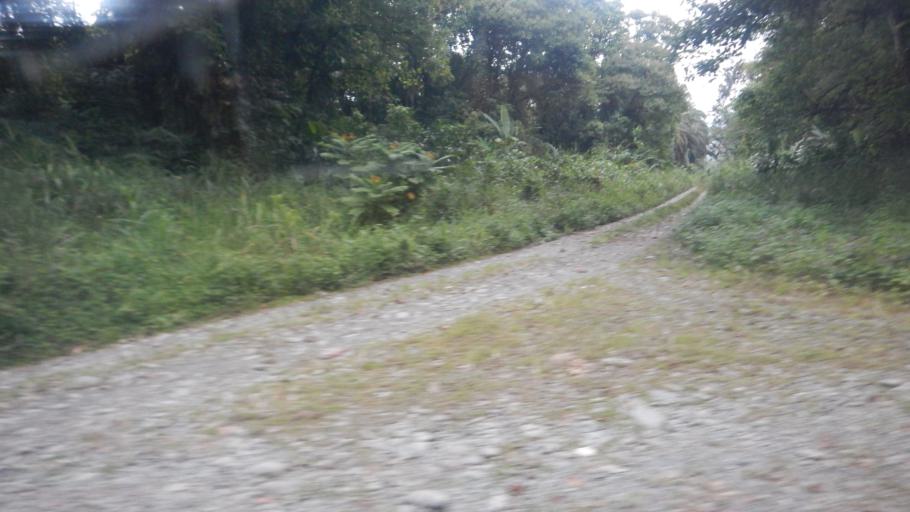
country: PG
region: Northern Province
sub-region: Sohe
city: Kokoda
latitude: -8.9187
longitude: 147.8949
